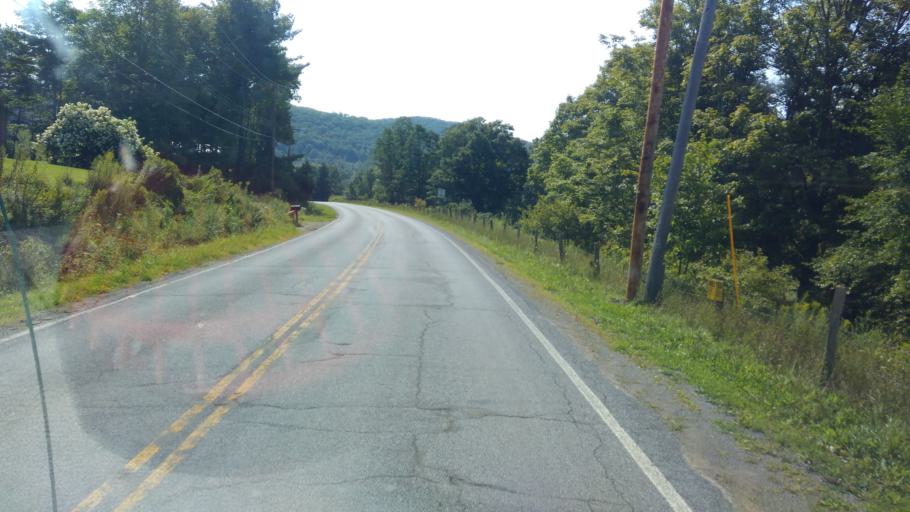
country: US
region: New York
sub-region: Allegany County
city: Bolivar
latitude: 42.0953
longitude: -78.1593
